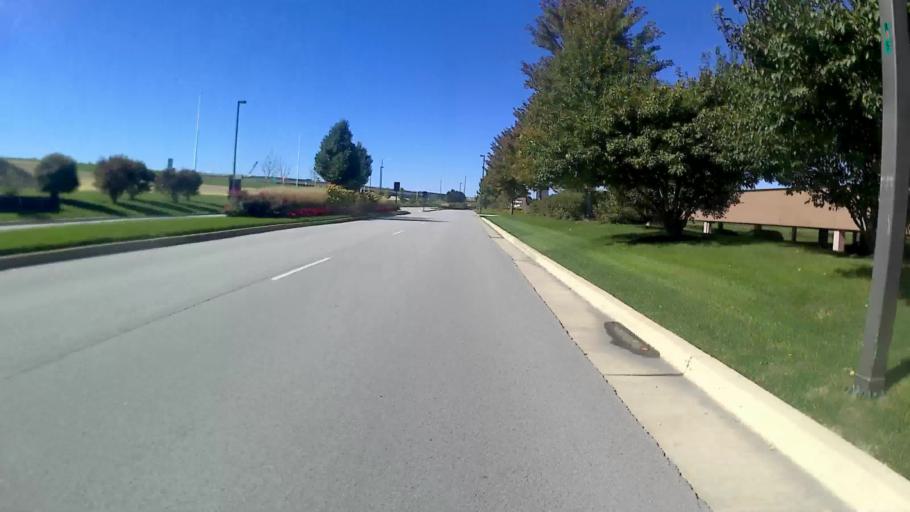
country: US
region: Illinois
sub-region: DuPage County
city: Itasca
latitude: 41.9852
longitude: -88.0187
